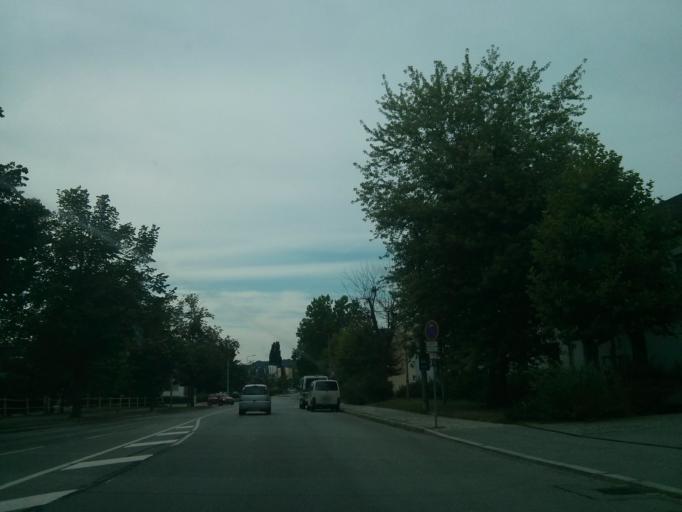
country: DE
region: Bavaria
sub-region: Lower Bavaria
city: Deggendorf
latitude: 48.8285
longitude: 12.9619
